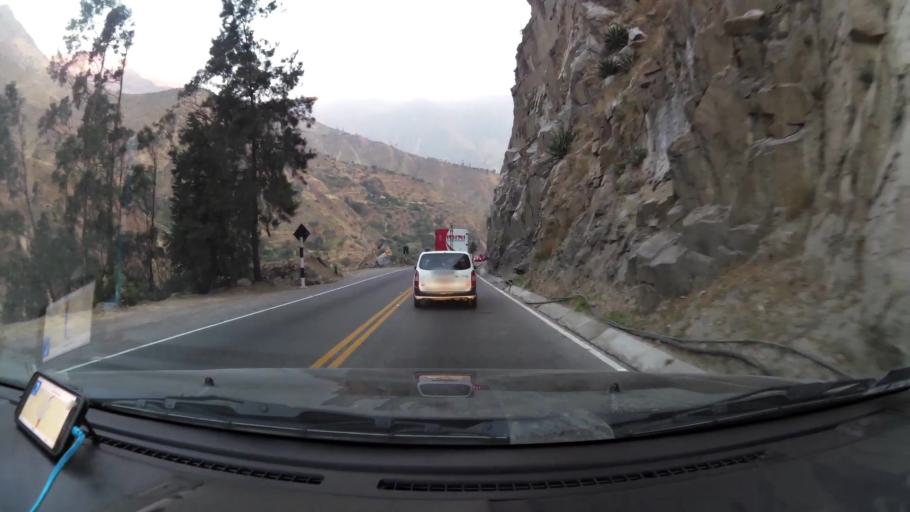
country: PE
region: Lima
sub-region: Provincia de Huarochiri
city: Surco
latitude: -11.8724
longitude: -76.4277
